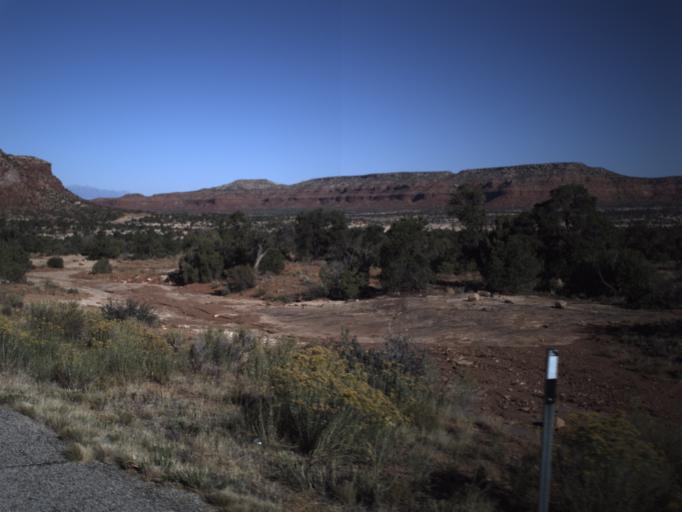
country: US
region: Utah
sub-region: San Juan County
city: Blanding
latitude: 37.6340
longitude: -110.0989
